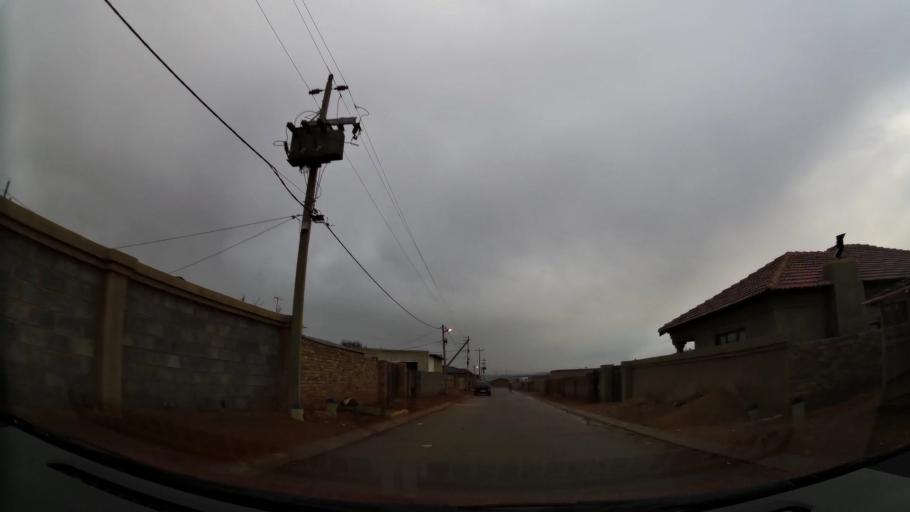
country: ZA
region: Gauteng
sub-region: West Rand District Municipality
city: Randfontein
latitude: -26.1746
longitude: 27.7806
